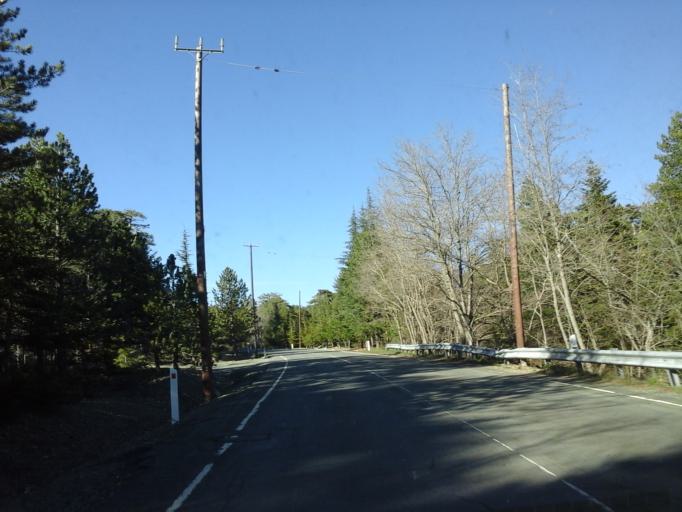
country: CY
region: Lefkosia
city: Kakopetria
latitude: 34.9336
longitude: 32.8892
